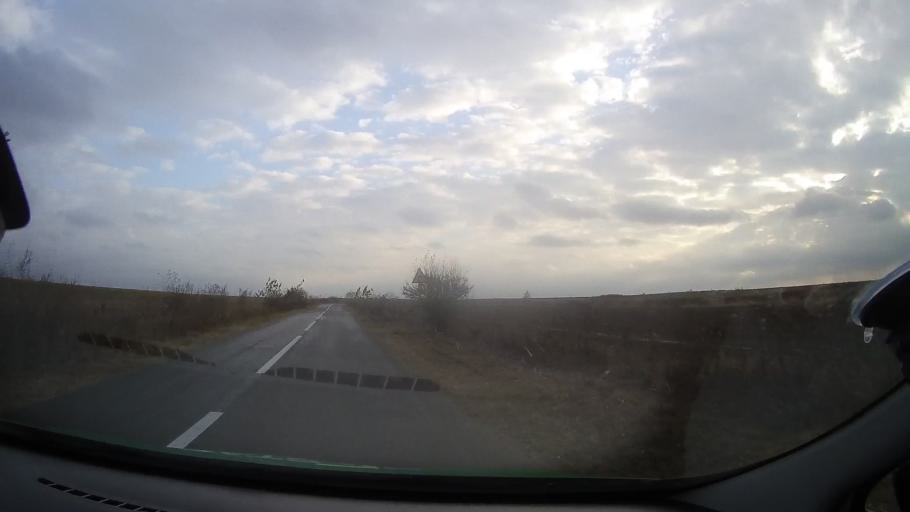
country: RO
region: Constanta
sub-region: Comuna Pestera
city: Pestera
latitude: 44.1348
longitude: 28.1190
